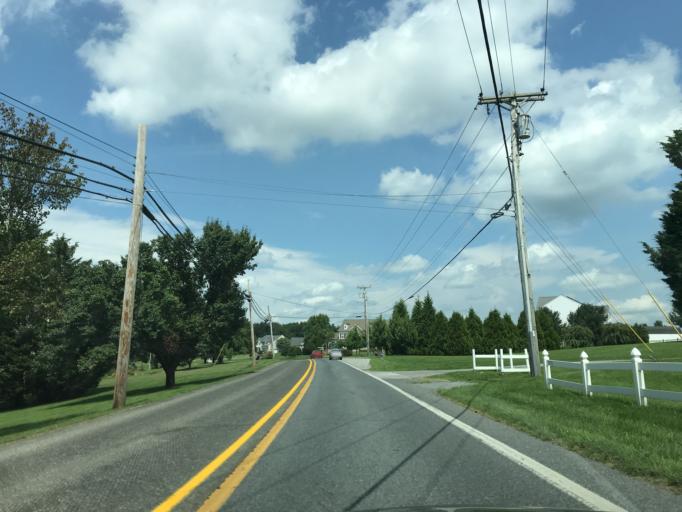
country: US
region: Pennsylvania
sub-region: York County
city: New Freedom
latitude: 39.6567
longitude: -76.7002
